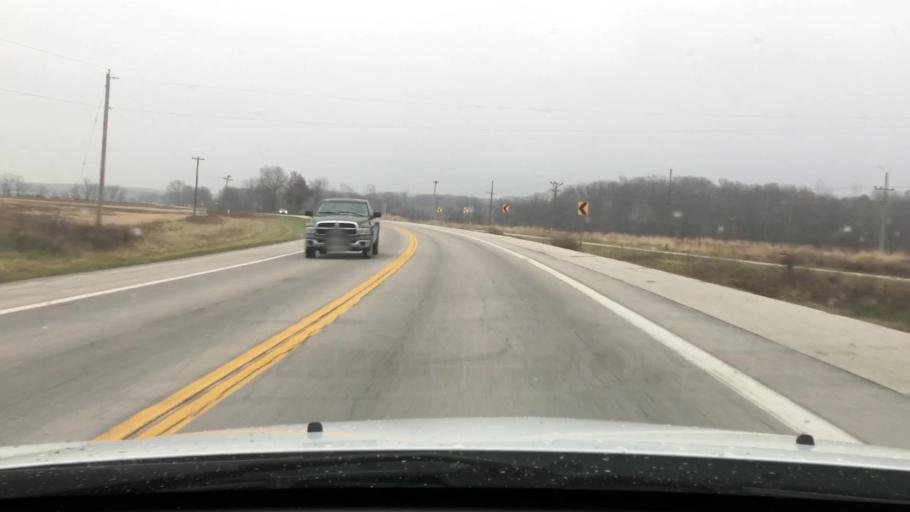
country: US
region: Missouri
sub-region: Pike County
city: Bowling Green
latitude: 39.3791
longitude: -91.1452
